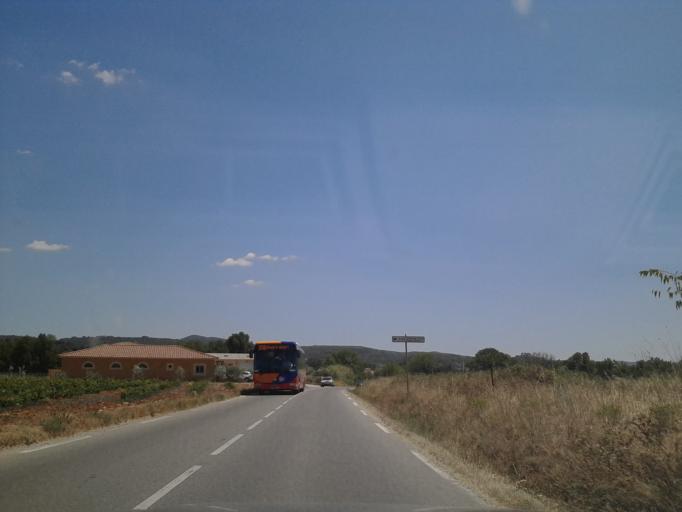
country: FR
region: Languedoc-Roussillon
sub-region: Departement de l'Herault
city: Aniane
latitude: 43.6972
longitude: 3.5770
